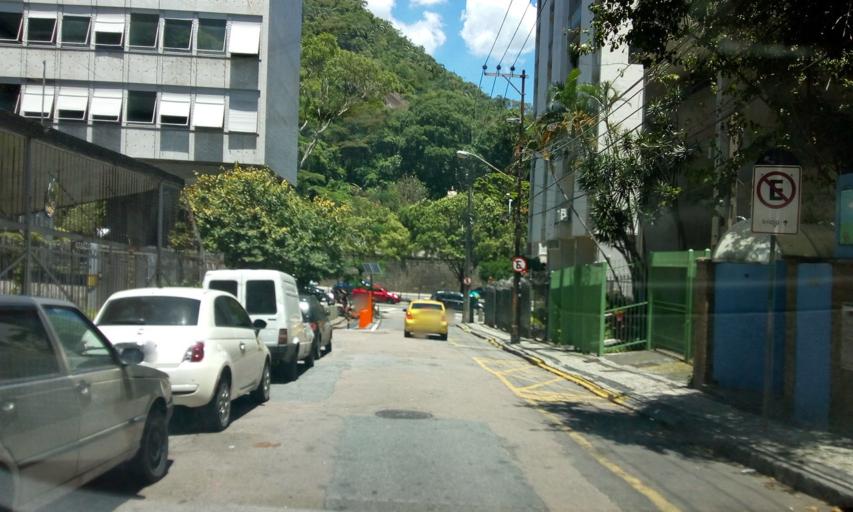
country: BR
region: Rio de Janeiro
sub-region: Rio De Janeiro
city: Rio de Janeiro
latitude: -22.9385
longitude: -43.1826
